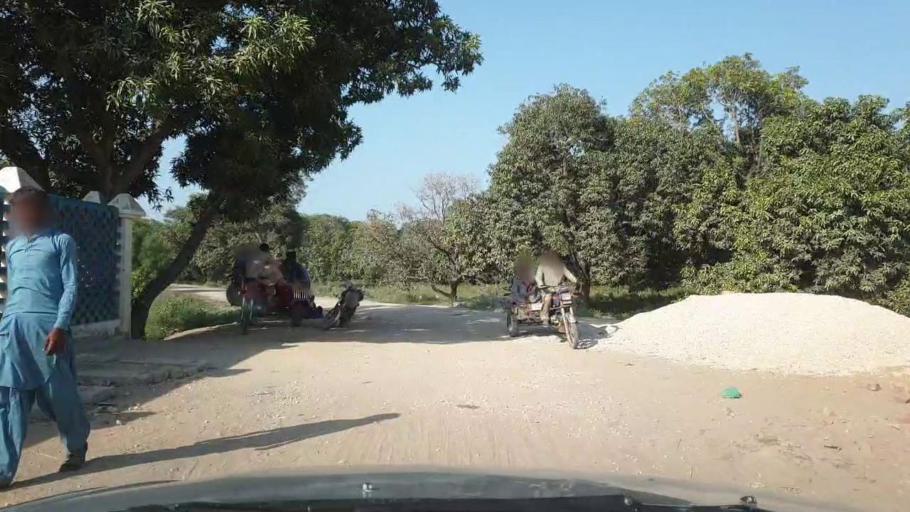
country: PK
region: Sindh
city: Tando Ghulam Ali
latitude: 25.1268
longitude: 68.8947
